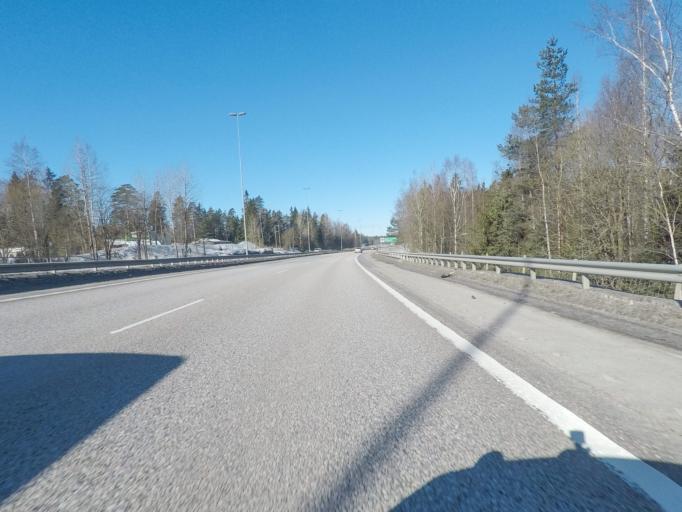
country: FI
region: Uusimaa
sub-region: Helsinki
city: Kirkkonummi
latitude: 60.2559
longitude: 24.5058
